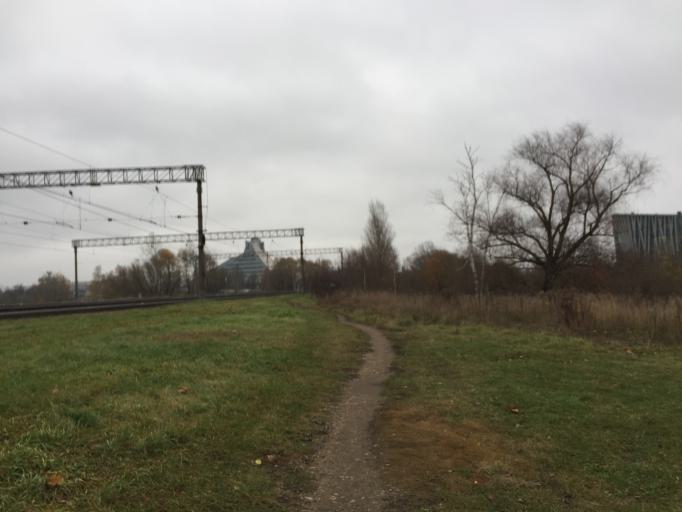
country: LV
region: Riga
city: Riga
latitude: 56.9353
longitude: 24.0923
